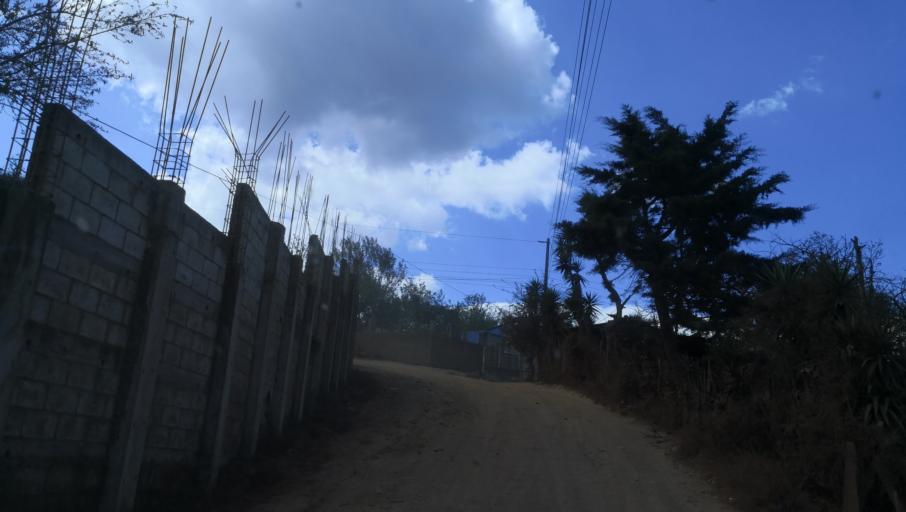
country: GT
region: Jalapa
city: San Carlos Alzatate
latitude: 14.3941
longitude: -89.9960
